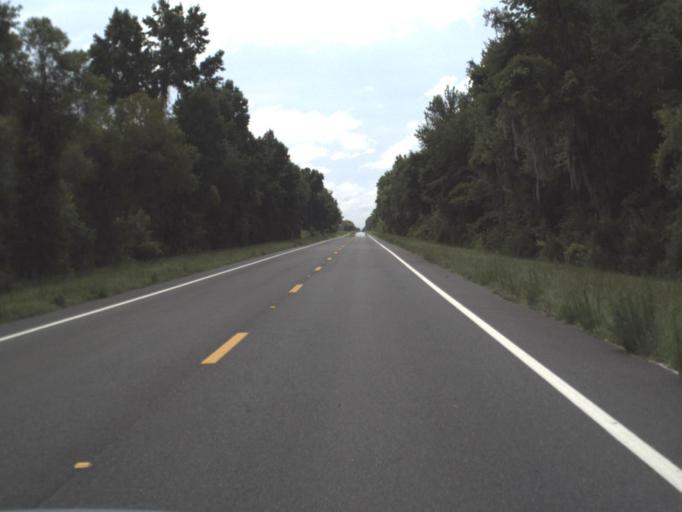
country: US
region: Florida
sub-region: Hamilton County
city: Jasper
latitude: 30.4649
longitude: -82.9011
